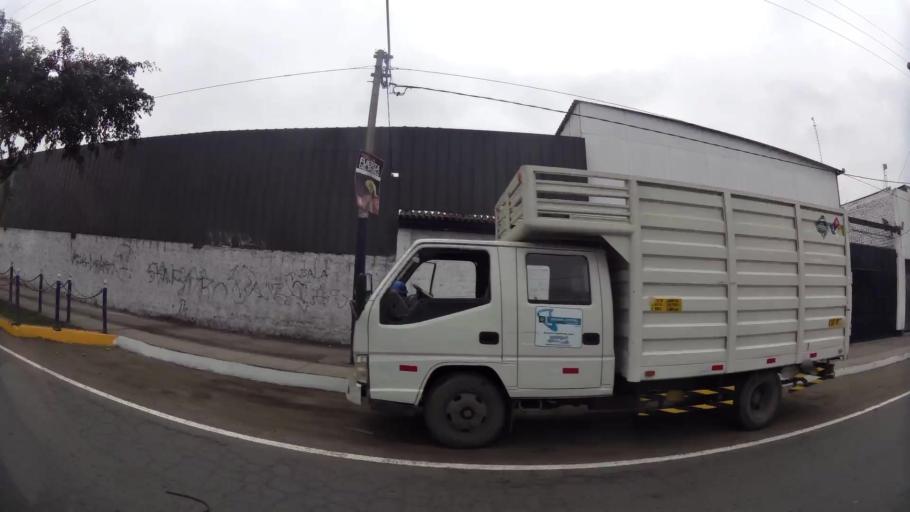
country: PE
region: Lima
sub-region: Lima
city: Surco
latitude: -12.1801
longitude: -76.9939
